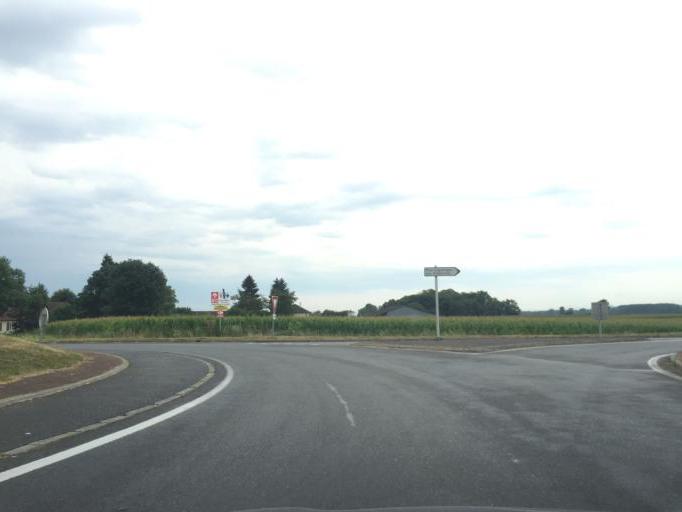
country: FR
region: Auvergne
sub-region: Departement de l'Allier
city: Varennes-sur-Allier
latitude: 46.3561
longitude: 3.3745
